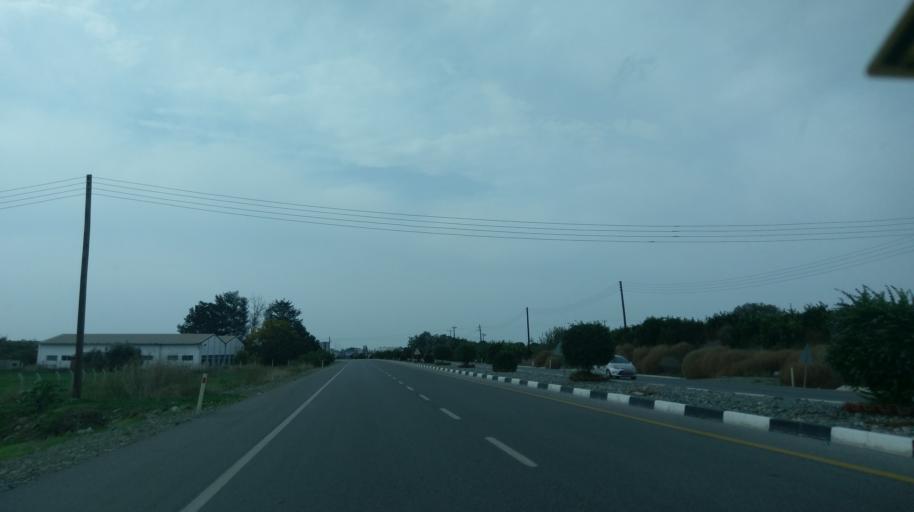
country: CY
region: Lefkosia
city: Morfou
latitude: 35.1972
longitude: 33.0161
